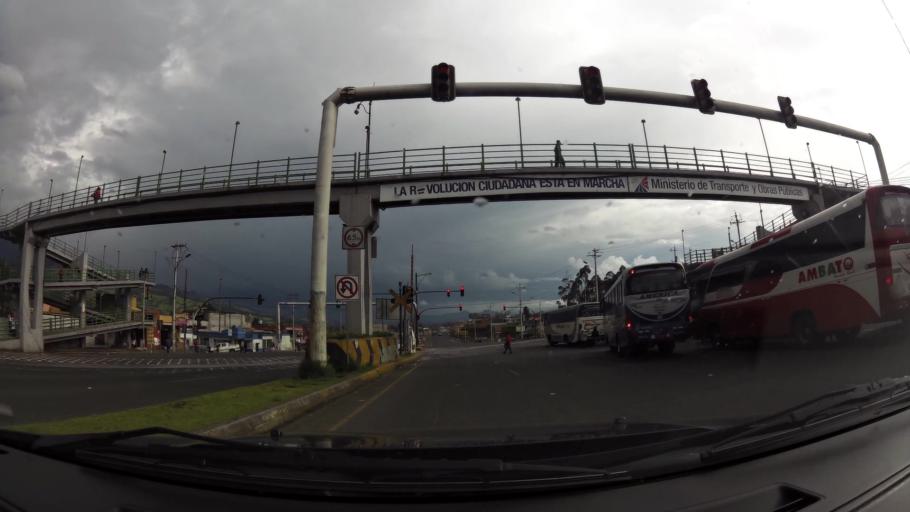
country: EC
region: Pichincha
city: Machachi
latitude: -0.4046
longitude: -78.5464
